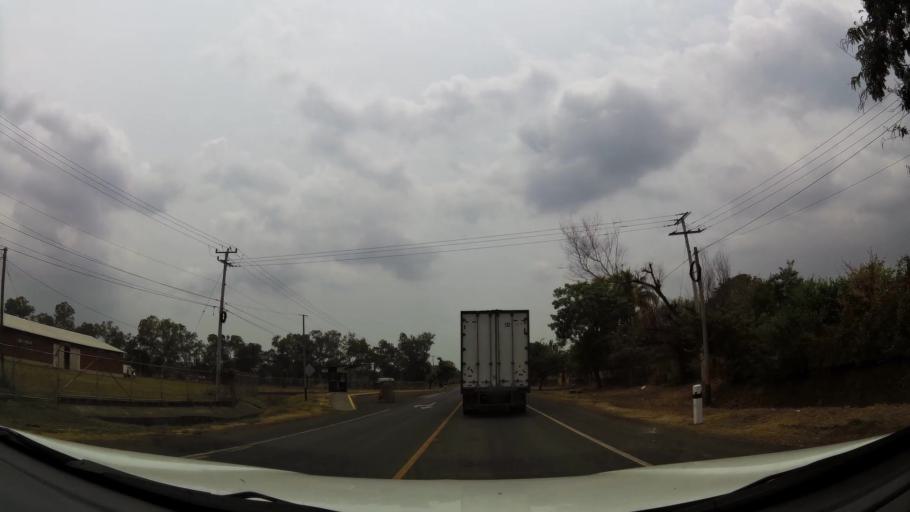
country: NI
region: Leon
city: Telica
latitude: 12.5239
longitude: -86.8737
